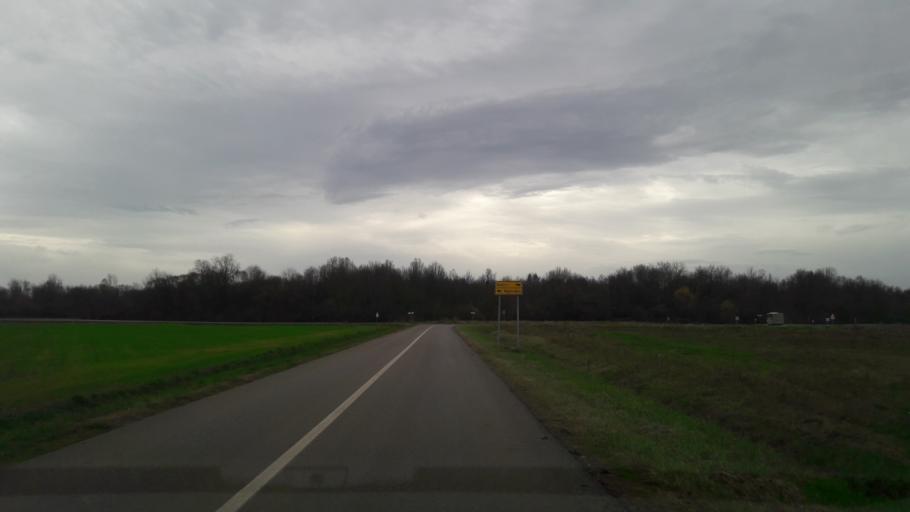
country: HR
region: Virovitick-Podravska
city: Zdenci
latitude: 45.6078
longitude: 18.0292
